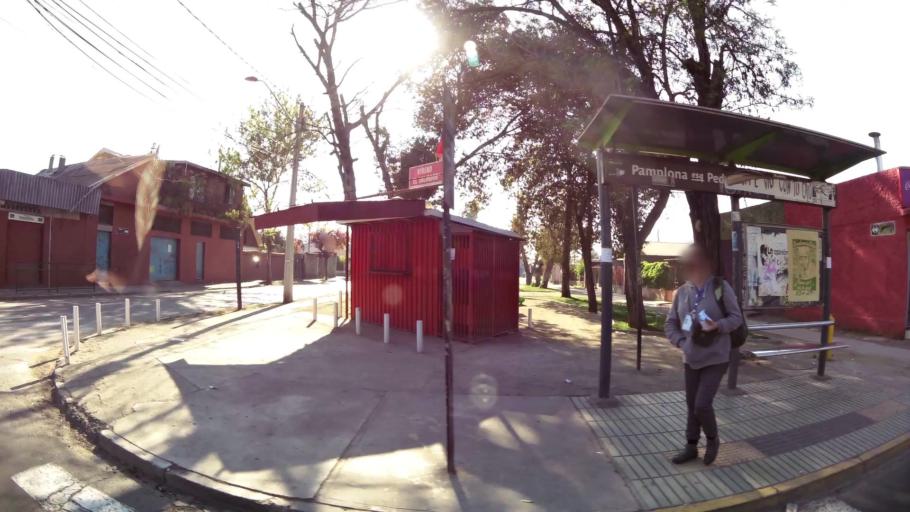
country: CL
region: Santiago Metropolitan
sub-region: Provincia de Santiago
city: Santiago
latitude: -33.3889
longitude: -70.6707
